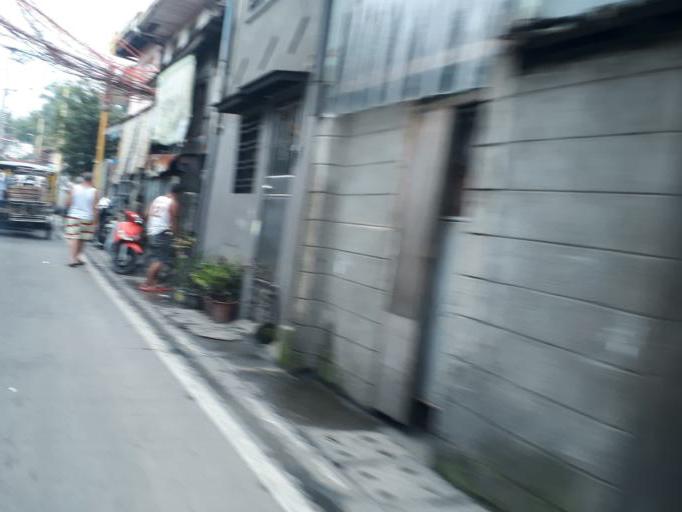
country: PH
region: Calabarzon
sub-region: Province of Rizal
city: Malabon
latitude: 14.6717
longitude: 120.9362
